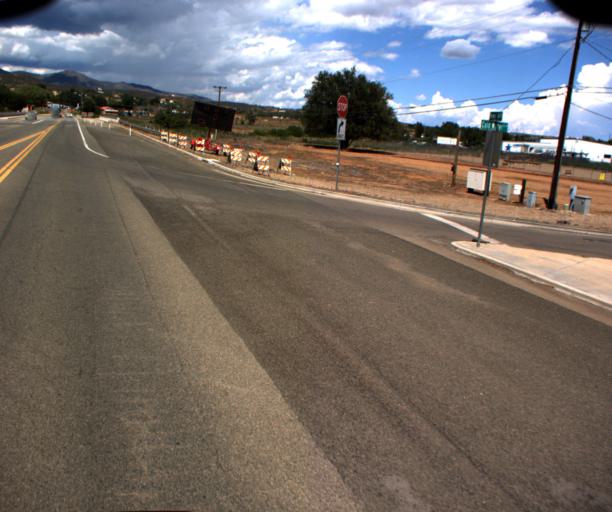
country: US
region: Arizona
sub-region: Yavapai County
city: Dewey-Humboldt
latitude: 34.5298
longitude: -112.2355
